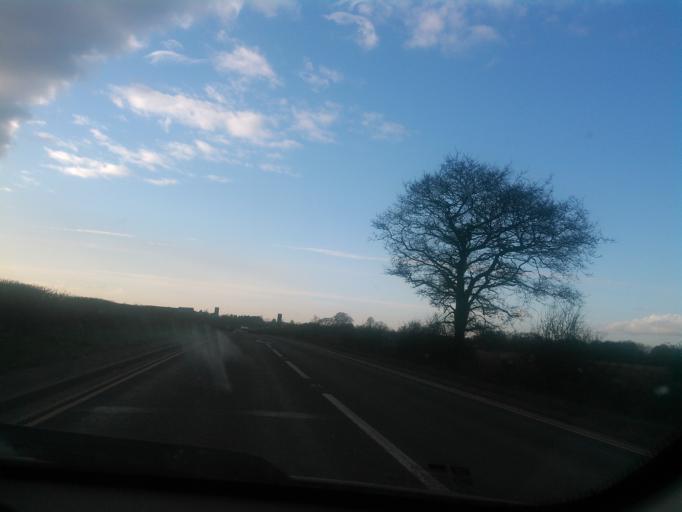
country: GB
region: England
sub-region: Shropshire
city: Stoke upon Tern
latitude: 52.8763
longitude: -2.5240
